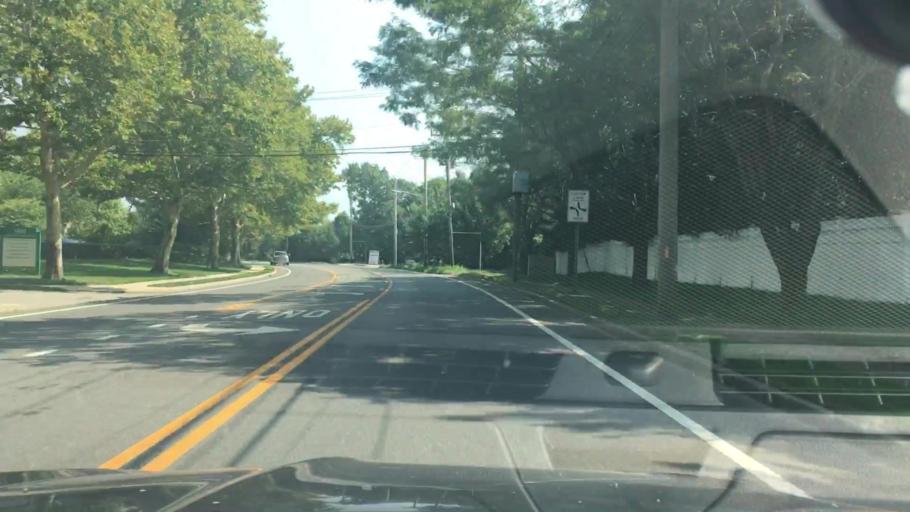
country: US
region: New York
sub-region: Nassau County
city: Old Bethpage
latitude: 40.7691
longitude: -73.4273
